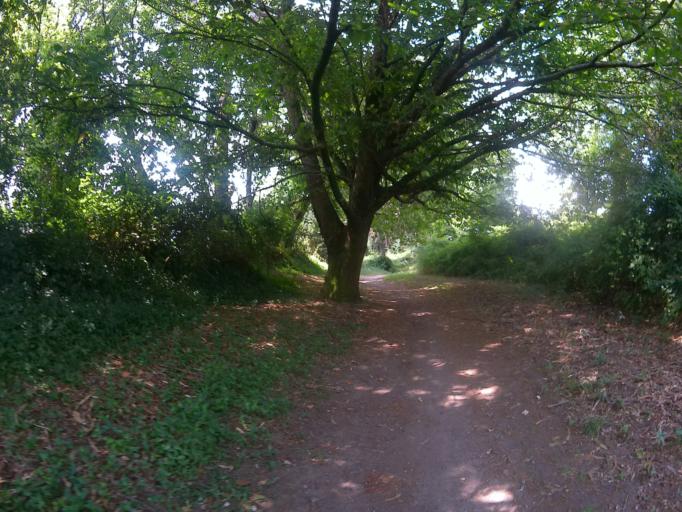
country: PT
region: Viana do Castelo
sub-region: Ponte de Lima
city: Ponte de Lima
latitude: 41.7763
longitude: -8.5839
